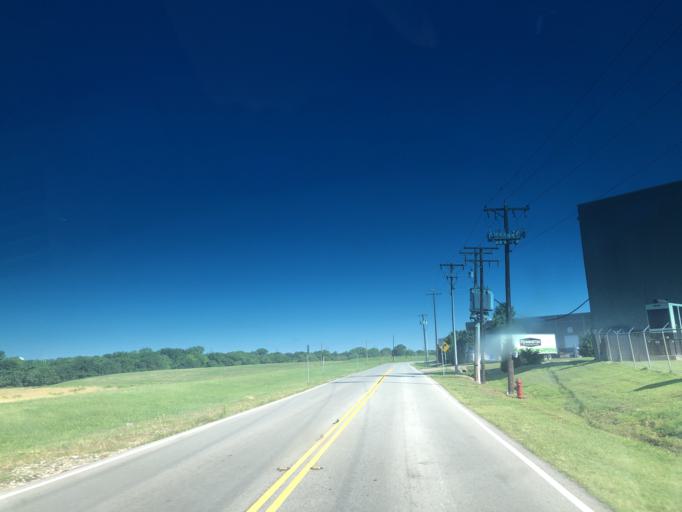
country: US
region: Texas
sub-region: Dallas County
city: Grand Prairie
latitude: 32.7304
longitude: -97.0215
